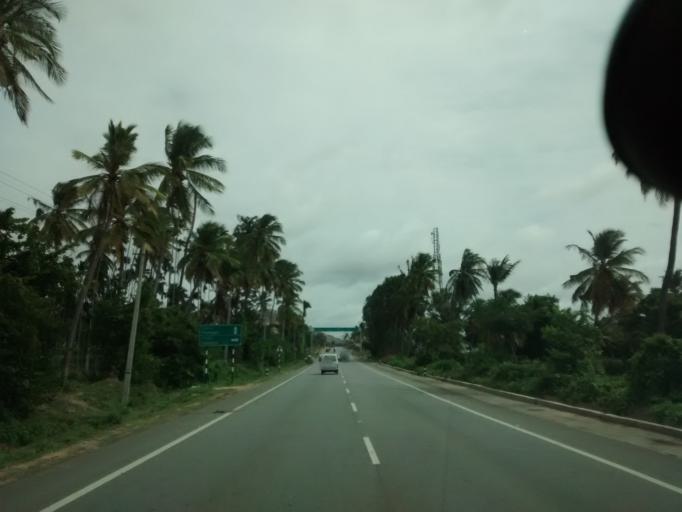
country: IN
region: Karnataka
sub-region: Tumkur
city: Koratagere
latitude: 13.5648
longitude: 77.2389
